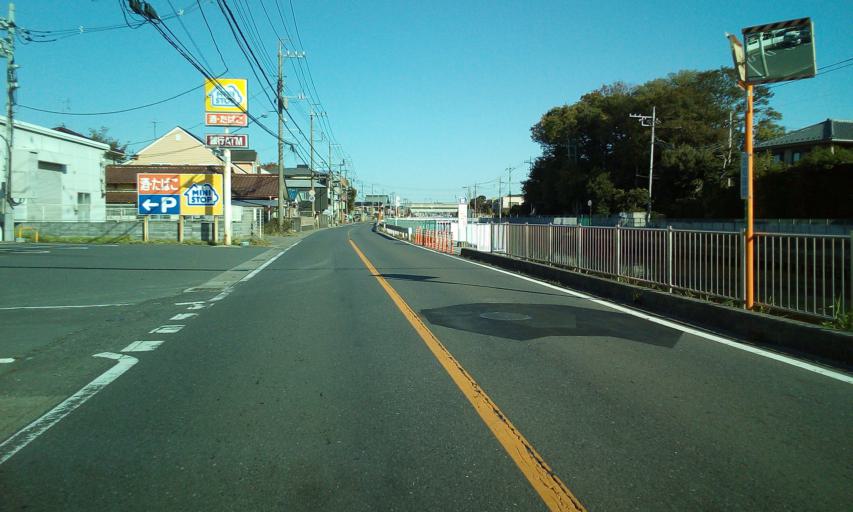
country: JP
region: Chiba
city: Nagareyama
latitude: 35.8253
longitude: 139.8829
